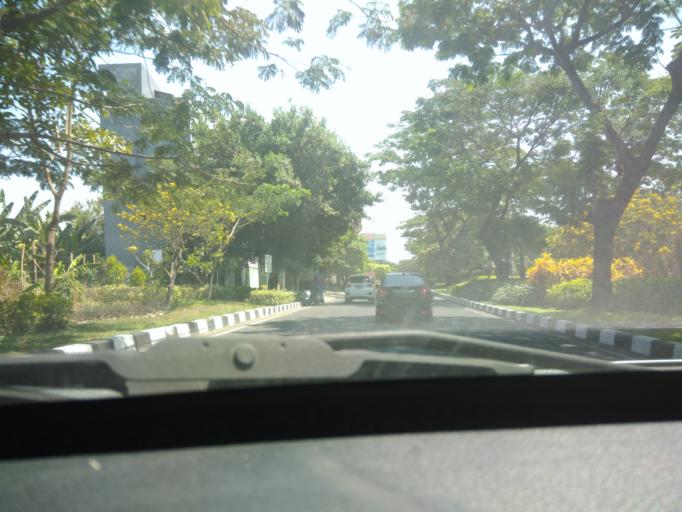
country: ID
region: East Java
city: Semampir
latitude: -7.3069
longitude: 112.7805
